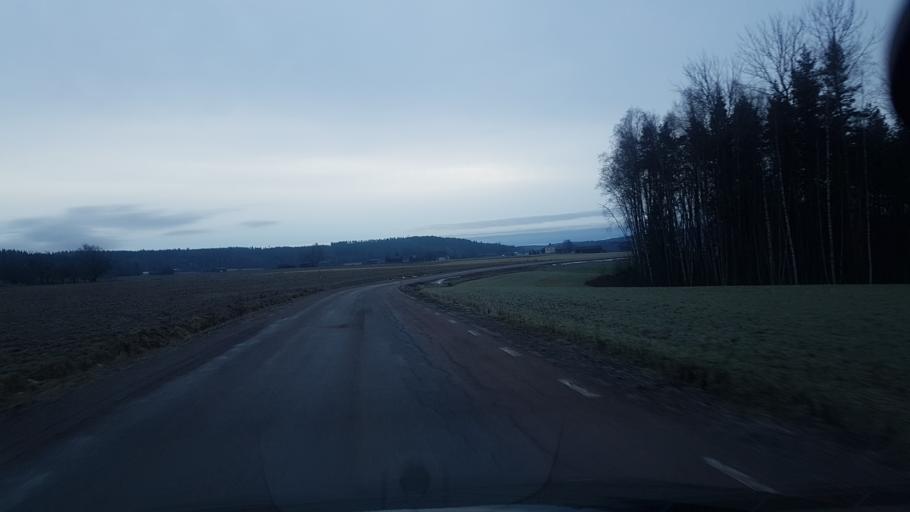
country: SE
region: Dalarna
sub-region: Saters Kommun
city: Saeter
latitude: 60.4356
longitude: 15.6555
